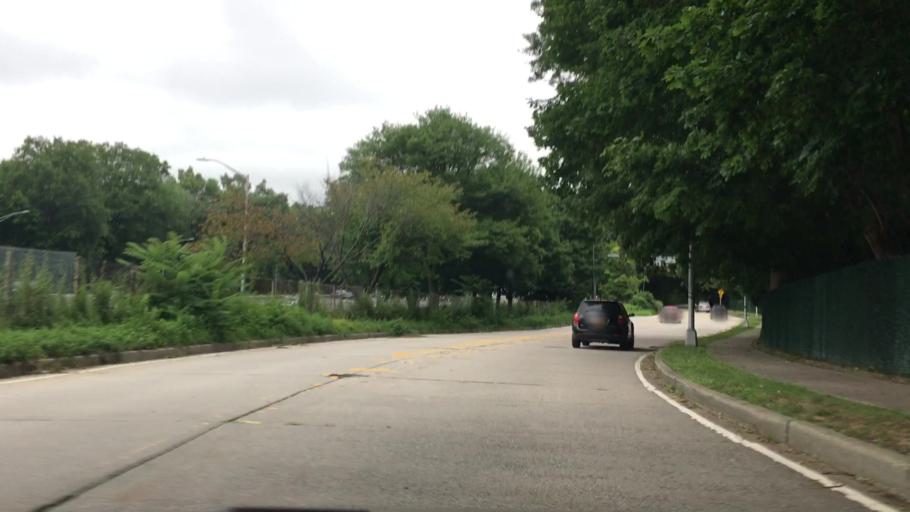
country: US
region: New York
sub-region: Nassau County
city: Lake Success
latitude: 40.7592
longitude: -73.7171
